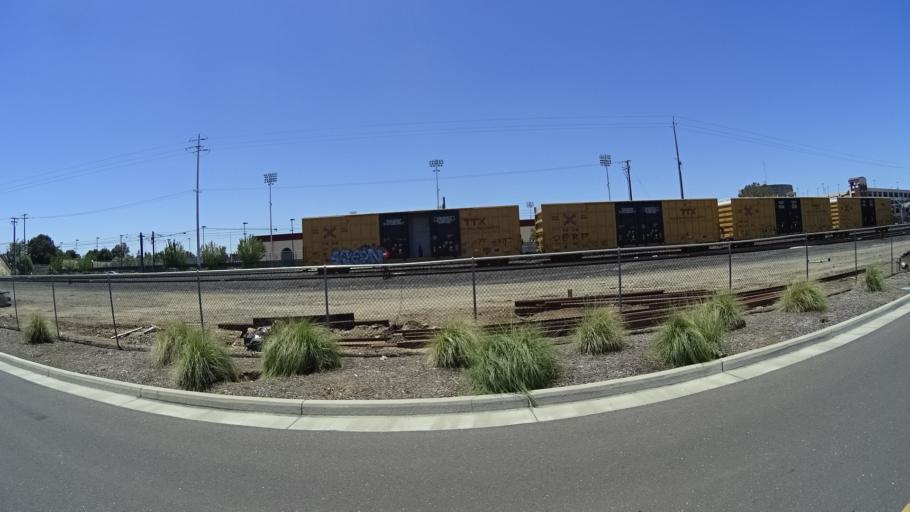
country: US
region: California
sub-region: Sacramento County
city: Sacramento
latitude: 38.5412
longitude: -121.4842
